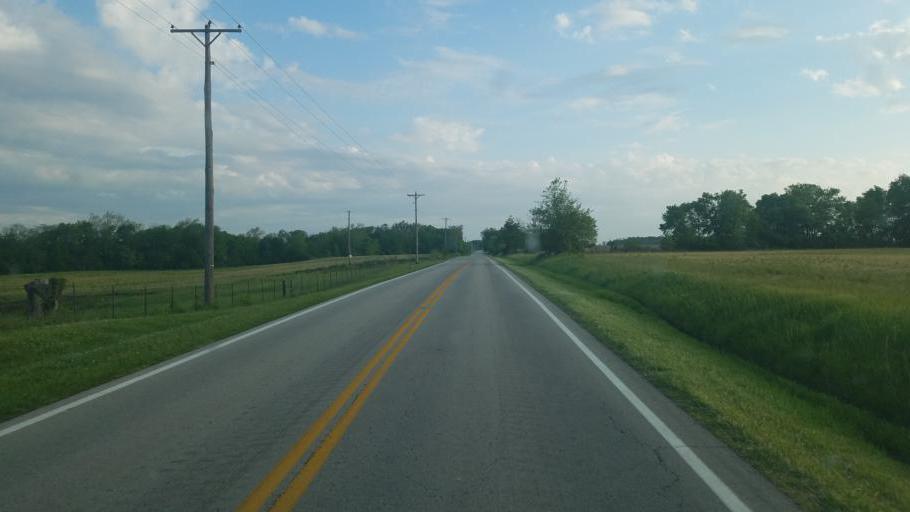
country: US
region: Ohio
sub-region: Highland County
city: Leesburg
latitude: 39.3772
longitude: -83.5939
